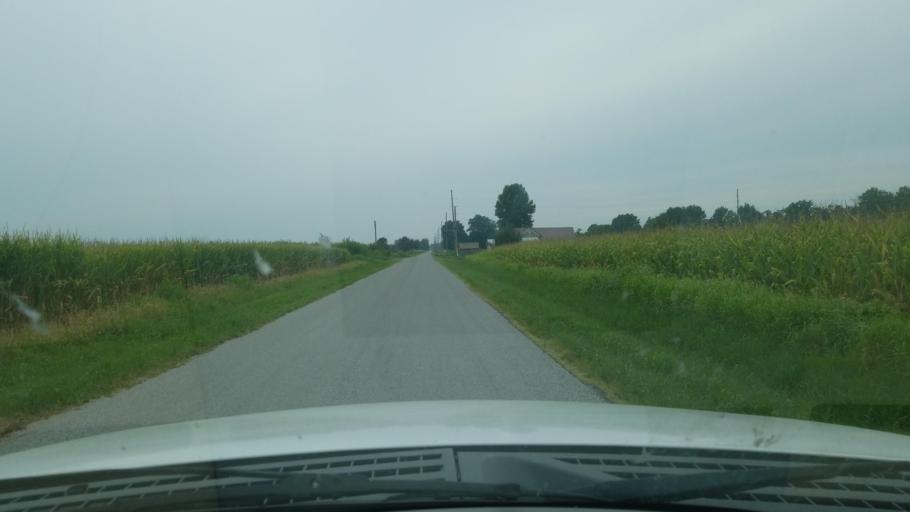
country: US
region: Illinois
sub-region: Saline County
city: Eldorado
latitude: 37.8631
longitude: -88.5014
